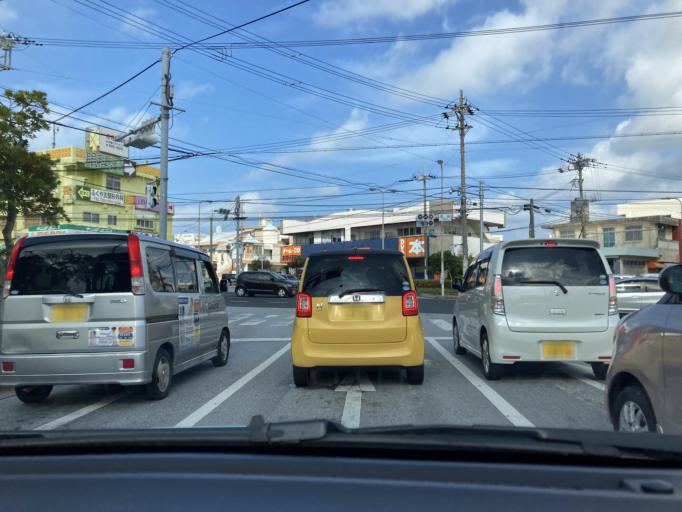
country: JP
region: Okinawa
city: Ginowan
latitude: 26.2624
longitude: 127.7618
